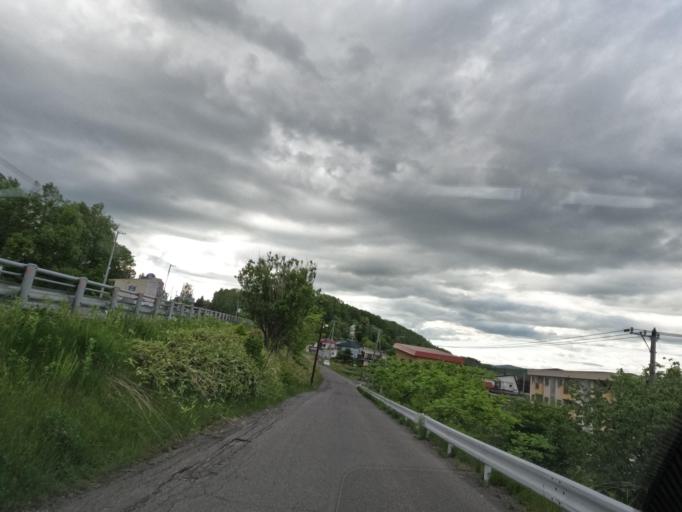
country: JP
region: Hokkaido
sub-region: Asahikawa-shi
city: Asahikawa
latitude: 43.7698
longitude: 142.3138
